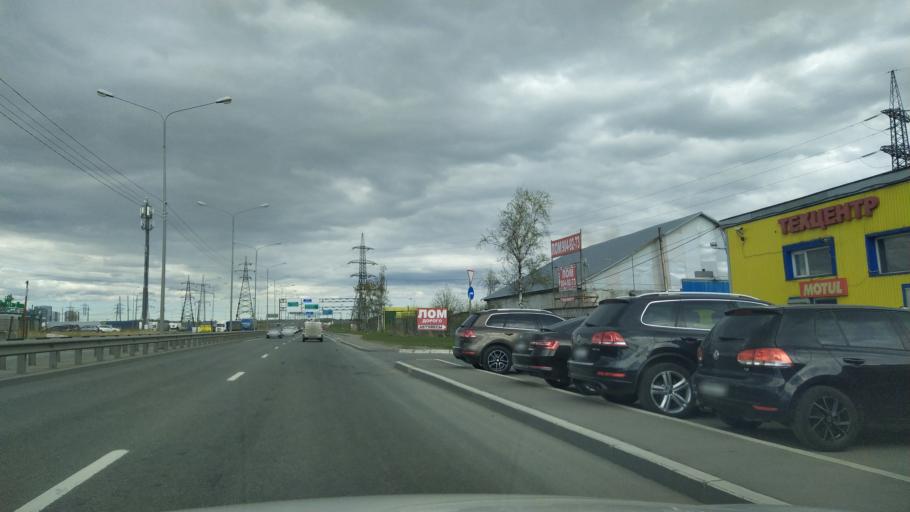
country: RU
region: Leningrad
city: Murino
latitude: 60.0111
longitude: 30.4543
